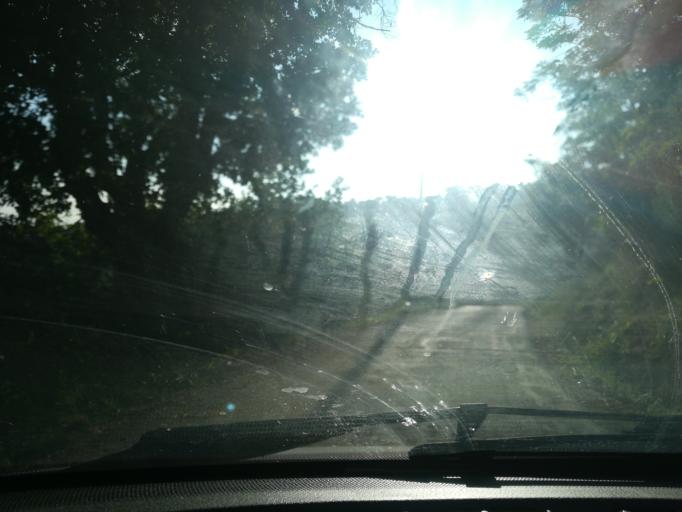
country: IT
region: The Marches
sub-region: Provincia di Macerata
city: Macerata
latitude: 43.2848
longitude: 13.4568
